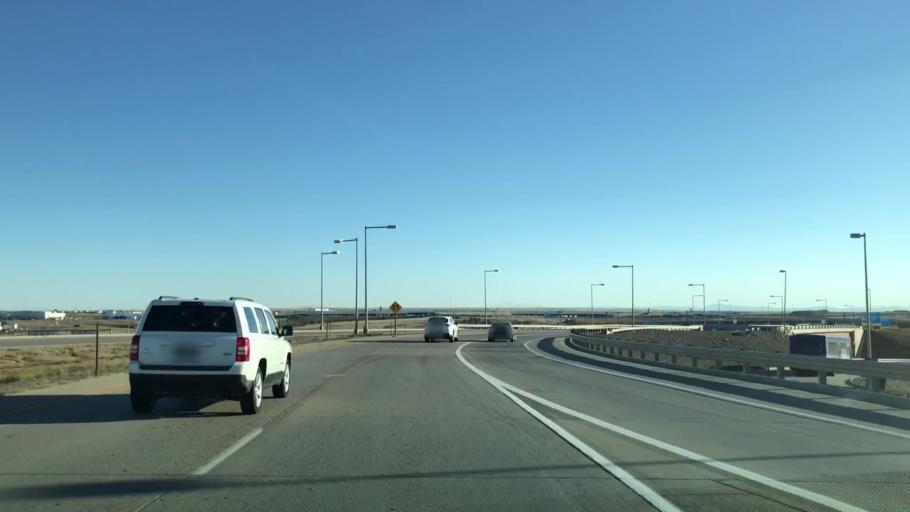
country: US
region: Colorado
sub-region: Weld County
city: Lochbuie
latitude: 39.8439
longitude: -104.6727
